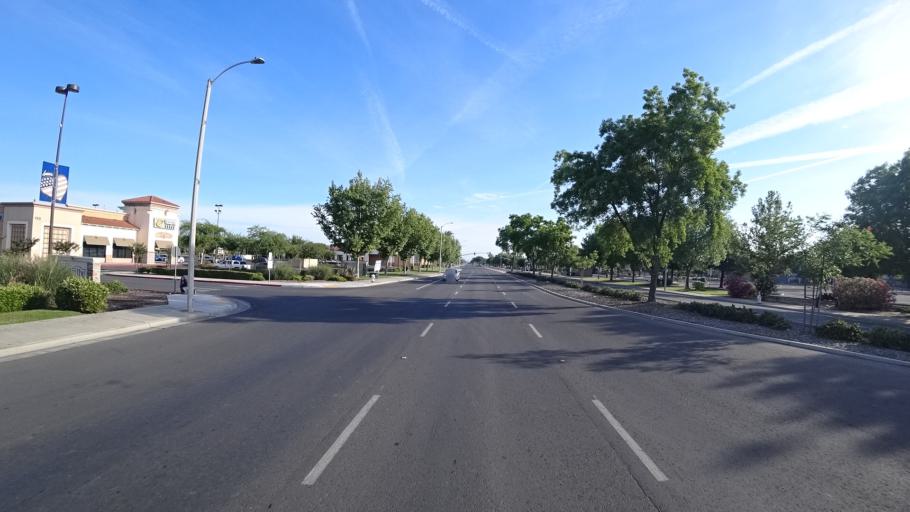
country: US
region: California
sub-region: Kings County
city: Hanford
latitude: 36.3237
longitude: -119.6730
